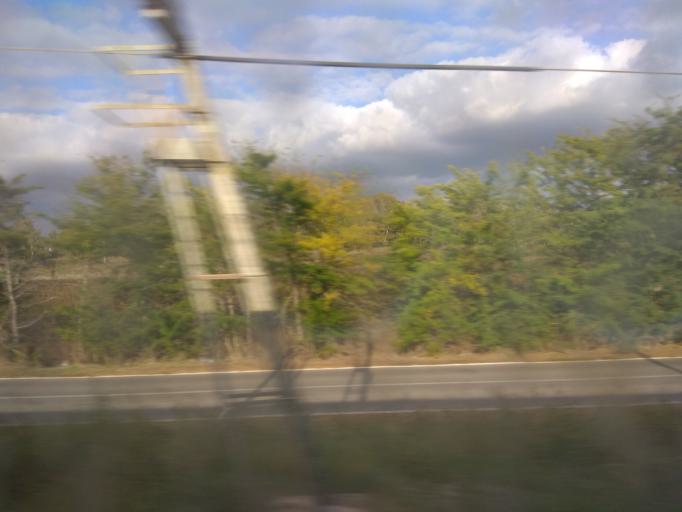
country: IT
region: Latium
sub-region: Citta metropolitana di Roma Capitale
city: Maccarese
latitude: 41.9110
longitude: 12.2052
